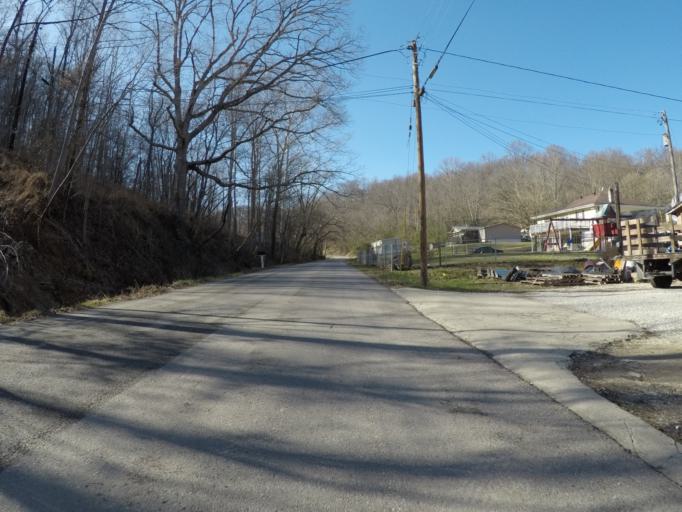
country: US
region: Kentucky
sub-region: Boyd County
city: Catlettsburg
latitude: 38.4041
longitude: -82.6252
